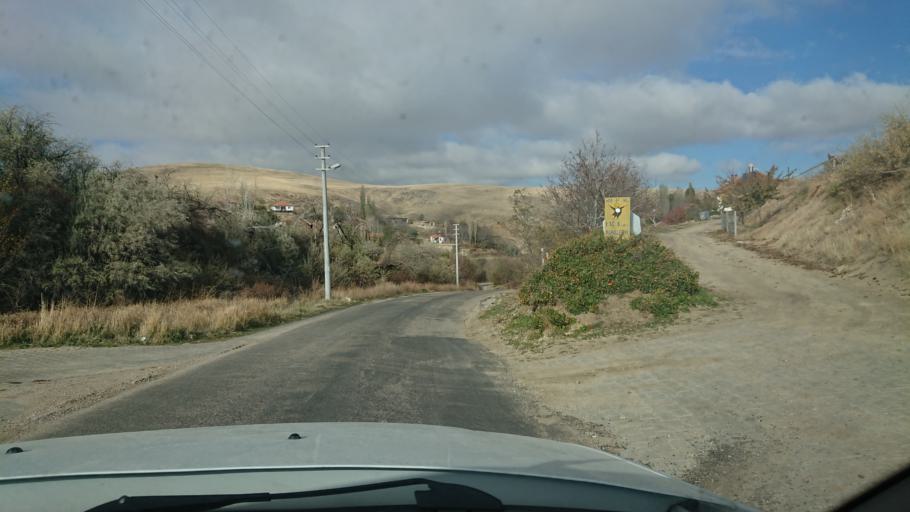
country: TR
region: Aksaray
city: Ortakoy
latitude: 38.8037
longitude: 33.9840
